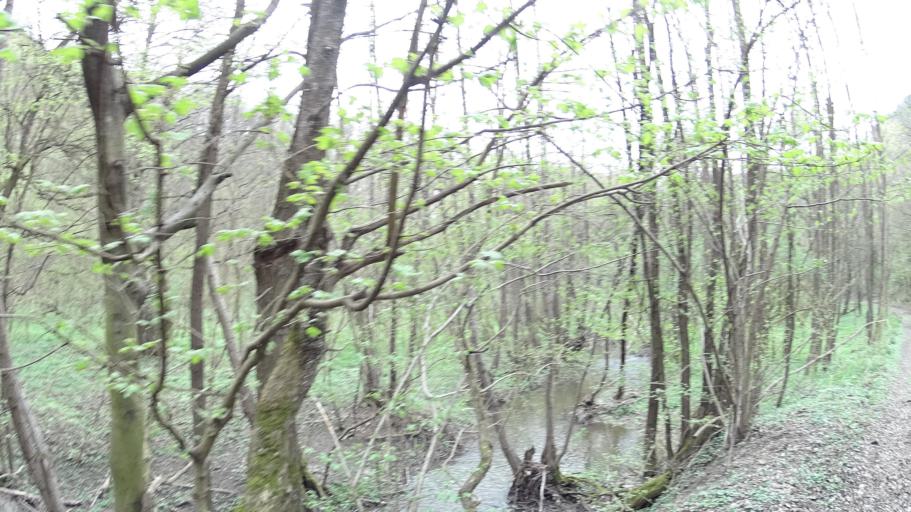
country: HU
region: Pest
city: Kismaros
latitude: 47.8830
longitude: 19.0311
